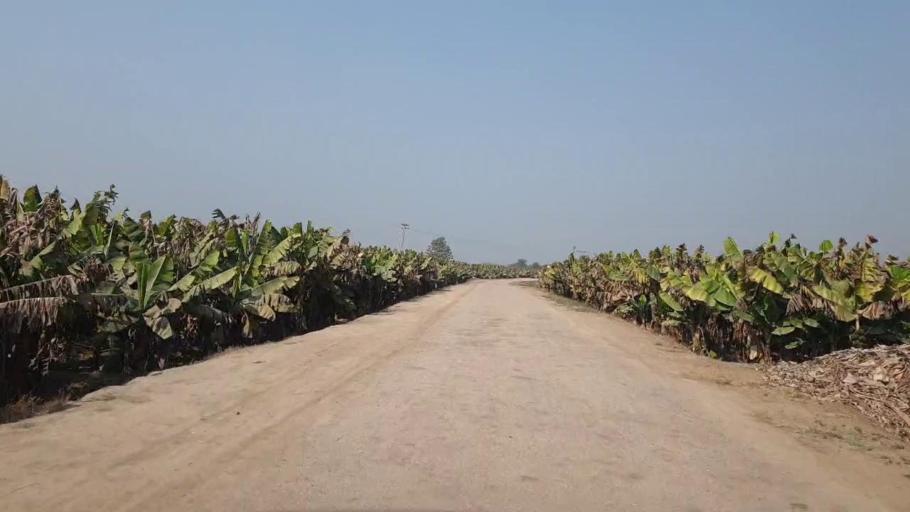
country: PK
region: Sindh
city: Bhit Shah
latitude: 25.7940
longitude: 68.4988
